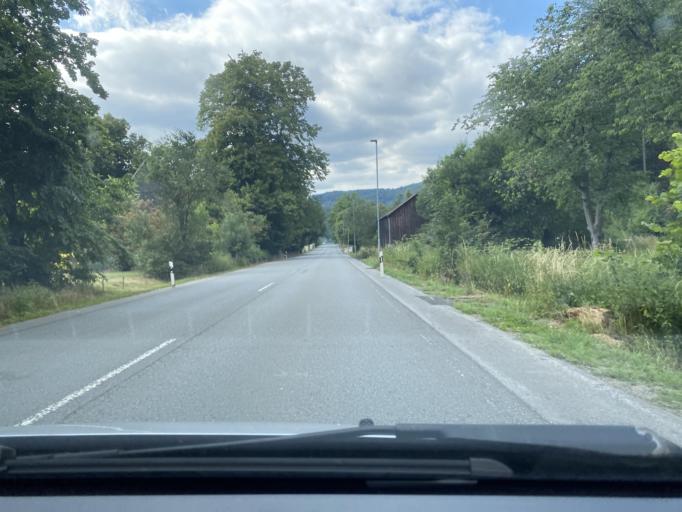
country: DE
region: North Rhine-Westphalia
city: Werdohl
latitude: 51.2691
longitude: 7.7231
